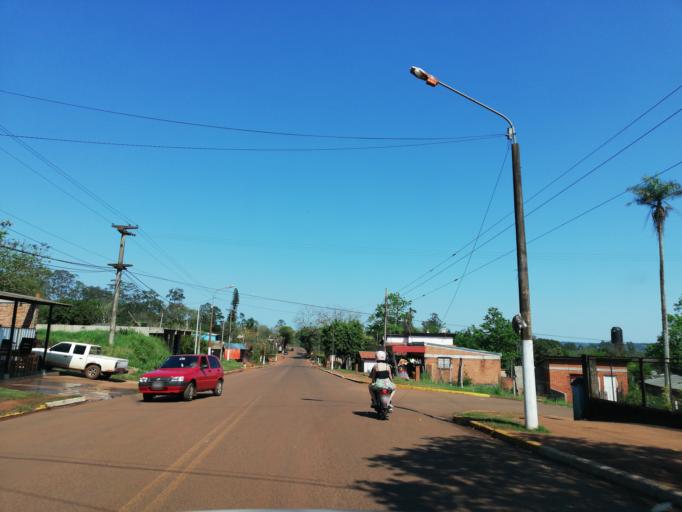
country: AR
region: Misiones
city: Puerto Eldorado
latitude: -26.4097
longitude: -54.6769
